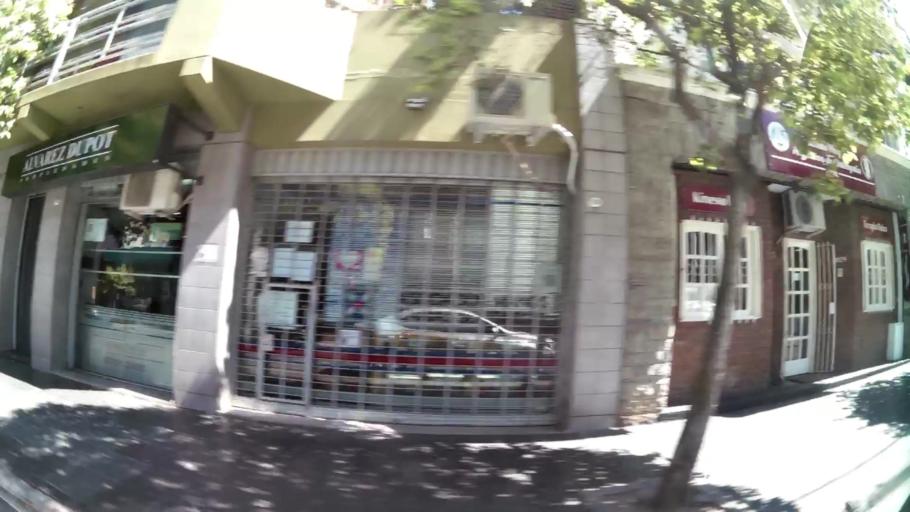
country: AR
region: Buenos Aires
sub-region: Partido de Vicente Lopez
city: Olivos
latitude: -34.5272
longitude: -58.4905
